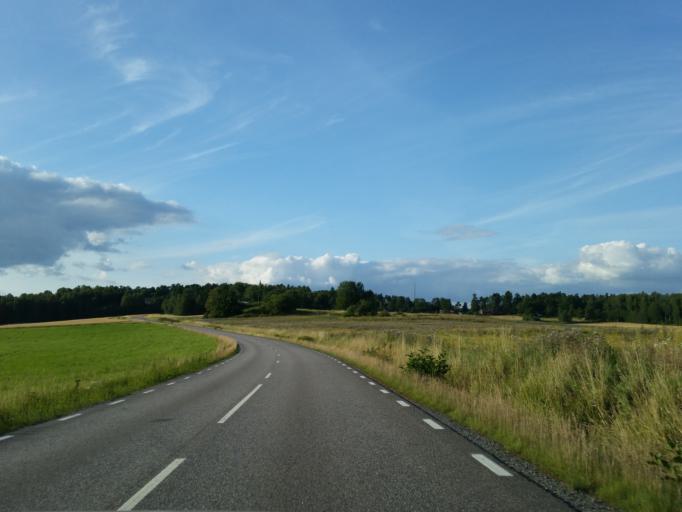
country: SE
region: Soedermanland
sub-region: Gnesta Kommun
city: Gnesta
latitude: 59.0229
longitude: 17.3607
